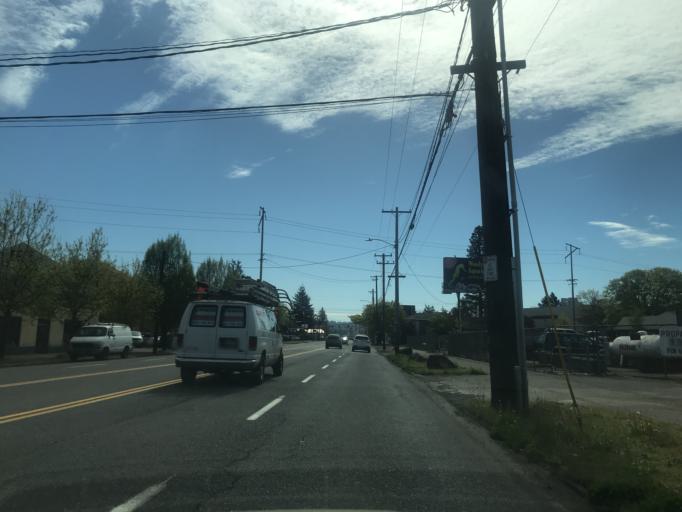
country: US
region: Oregon
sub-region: Multnomah County
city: Lents
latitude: 45.4878
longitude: -122.5925
